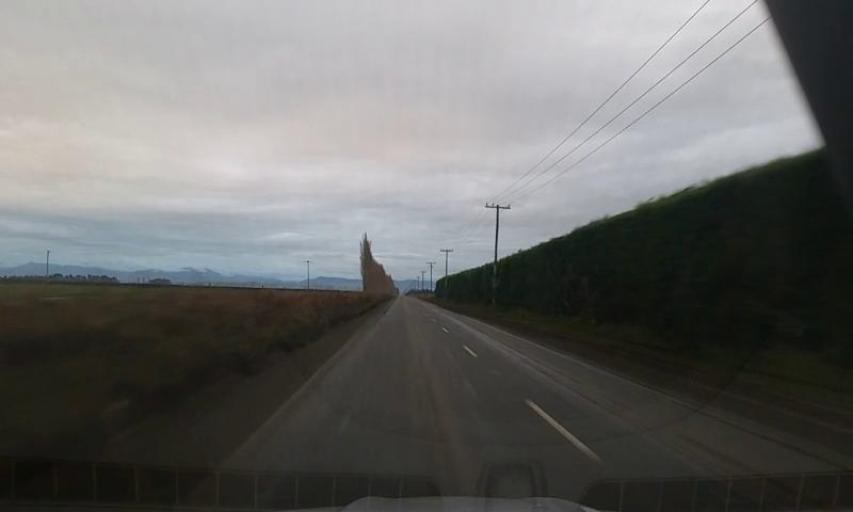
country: NZ
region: Canterbury
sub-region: Ashburton District
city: Methven
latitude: -43.7419
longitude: 171.7126
